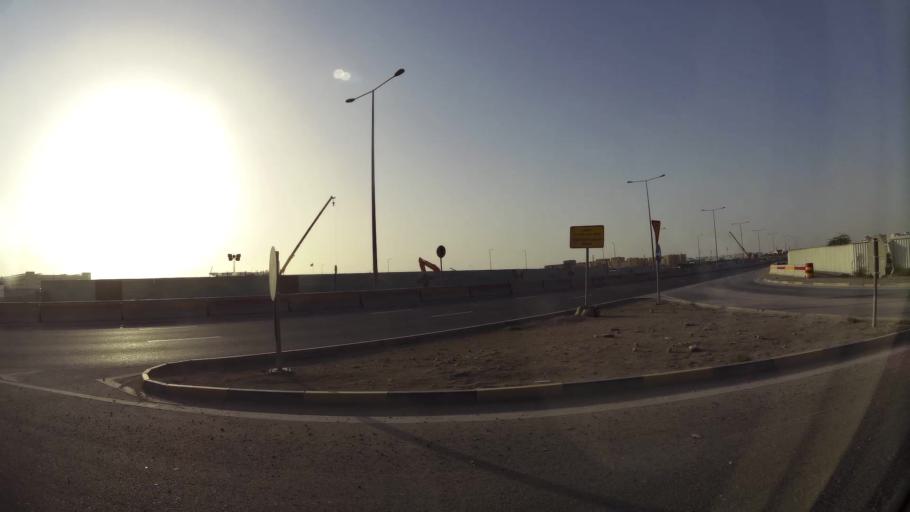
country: QA
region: Baladiyat ar Rayyan
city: Ar Rayyan
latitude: 25.3253
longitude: 51.4483
